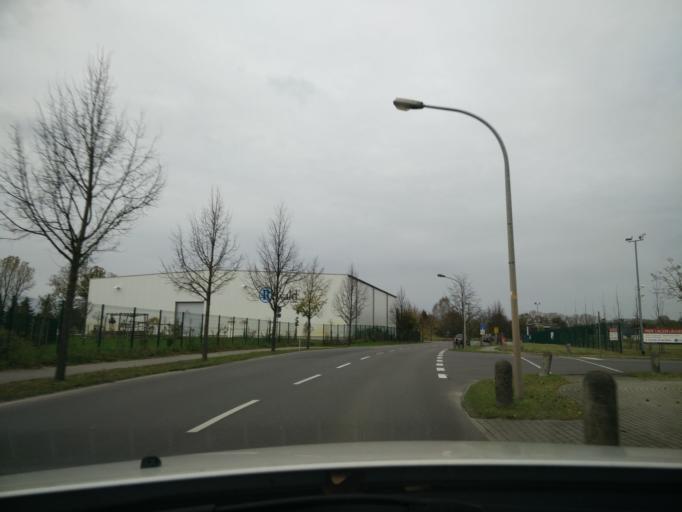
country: DE
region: Brandenburg
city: Velten
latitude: 52.6826
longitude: 13.1928
